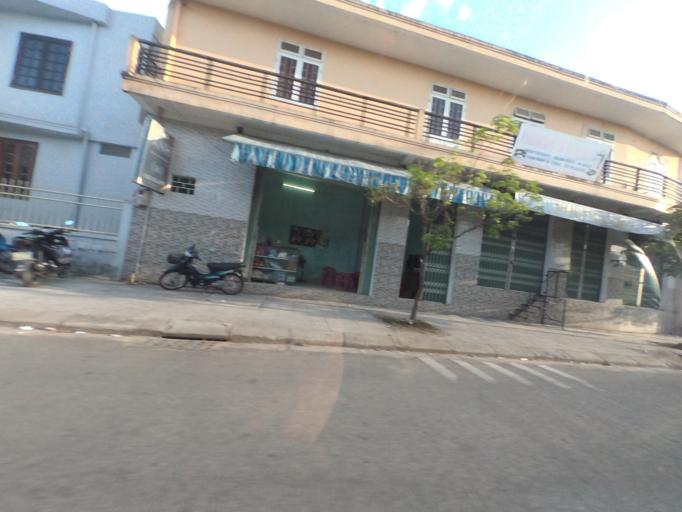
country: VN
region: Thua Thien-Hue
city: Hue
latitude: 16.4886
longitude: 107.5878
